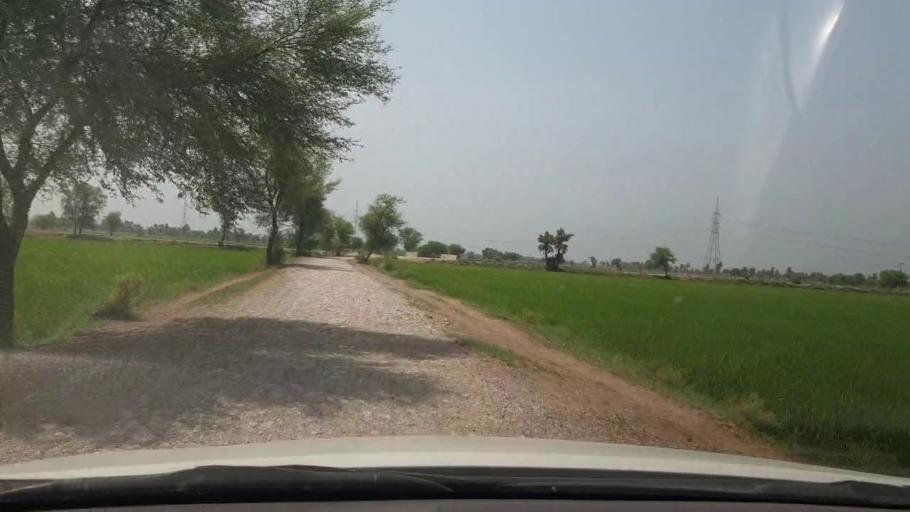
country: PK
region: Sindh
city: Shikarpur
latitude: 28.0154
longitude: 68.6499
